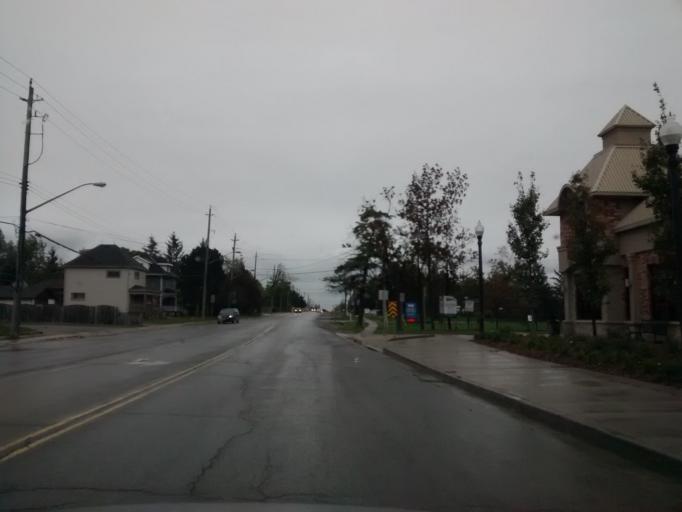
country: CA
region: Ontario
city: Hamilton
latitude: 43.1212
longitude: -79.8044
